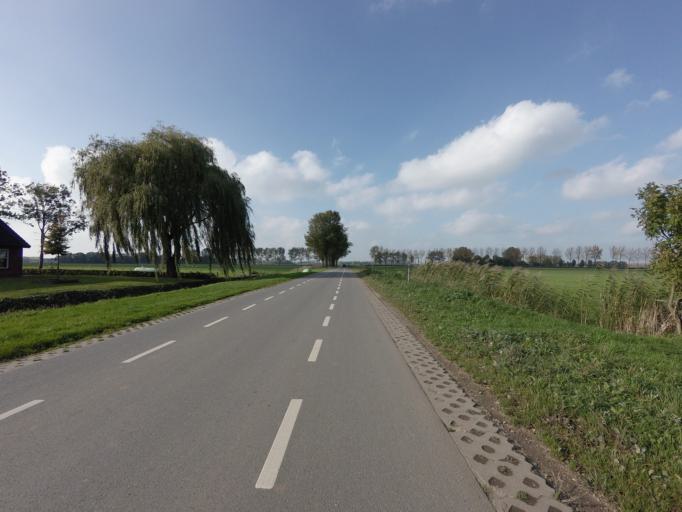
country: NL
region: Gelderland
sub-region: Gemeente Geldermalsen
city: Geldermalsen
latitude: 51.9205
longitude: 5.2889
